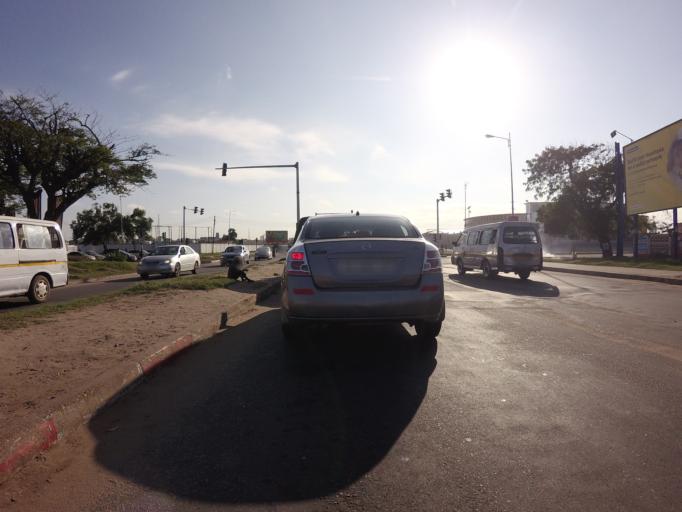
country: GH
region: Greater Accra
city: Accra
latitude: 5.5370
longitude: -0.2222
